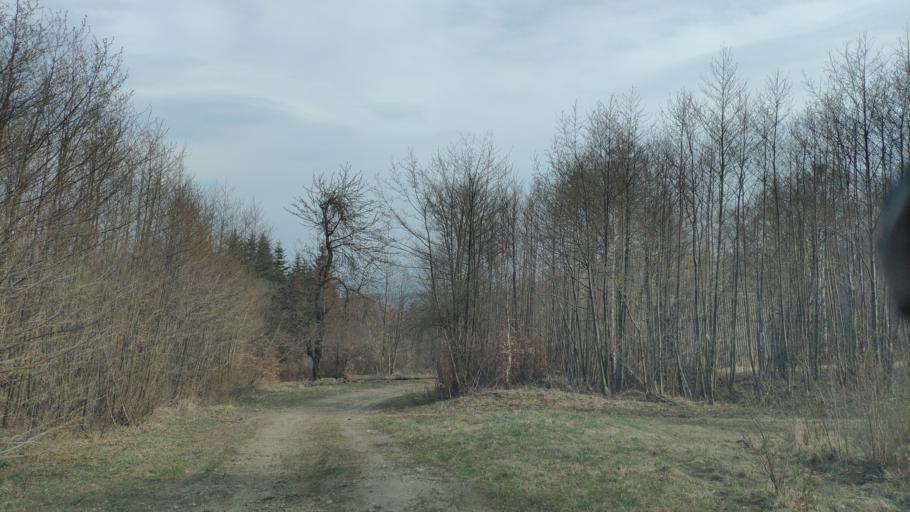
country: SK
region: Kosicky
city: Moldava nad Bodvou
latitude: 48.7414
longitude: 21.0529
